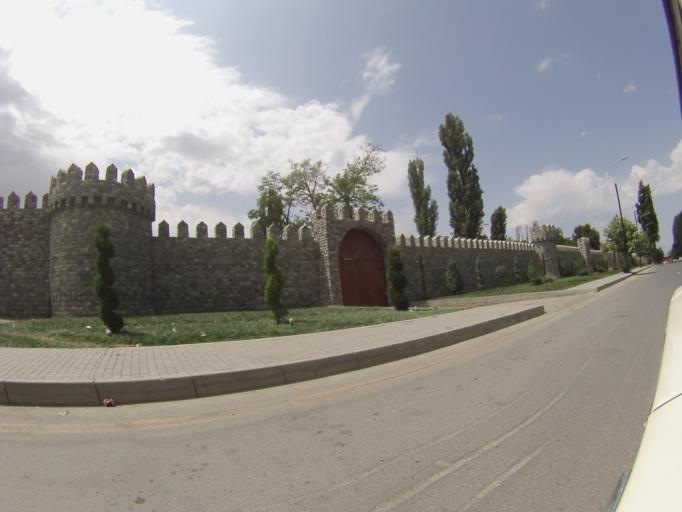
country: AZ
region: Ismayilli
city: Ismayilli
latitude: 40.7863
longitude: 48.1762
